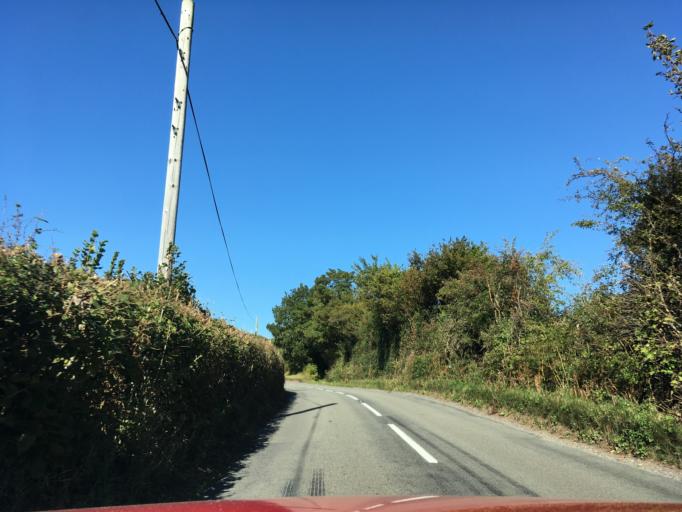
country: GB
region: Wales
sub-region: Torfaen County Borough
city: Cwmbran
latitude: 51.6282
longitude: -3.0505
